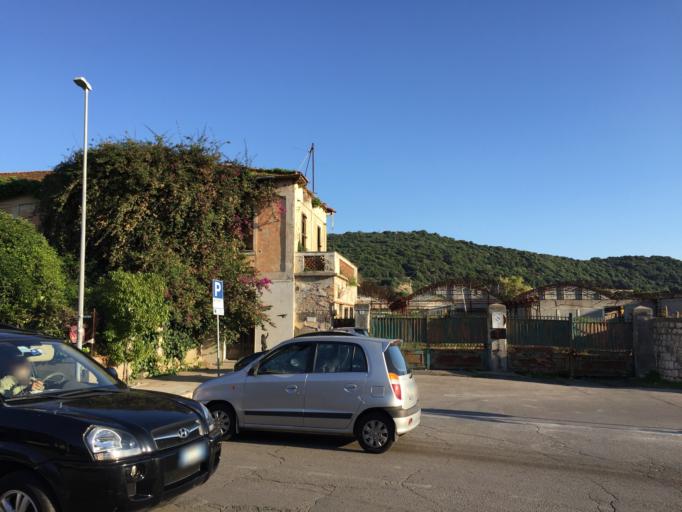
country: IT
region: Latium
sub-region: Provincia di Latina
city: Gaeta
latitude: 41.2135
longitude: 13.5673
